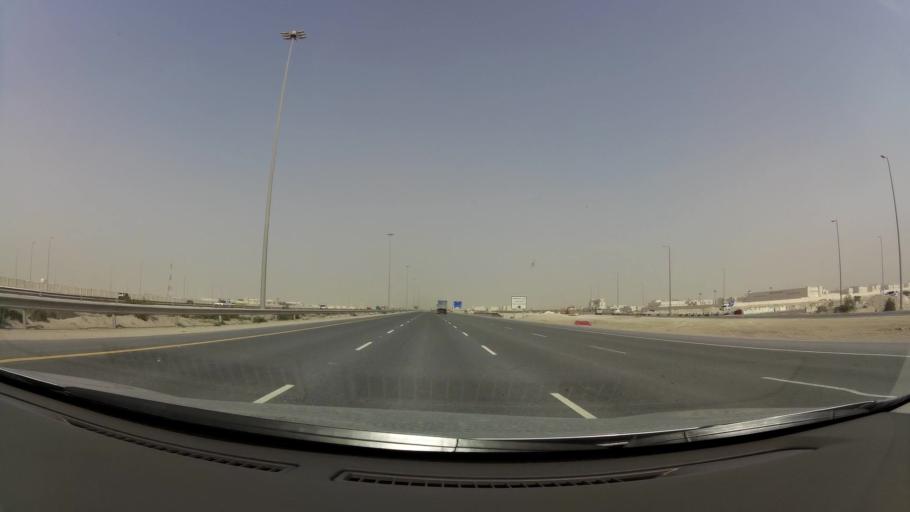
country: QA
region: Baladiyat ar Rayyan
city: Ar Rayyan
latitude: 25.1816
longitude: 51.3522
